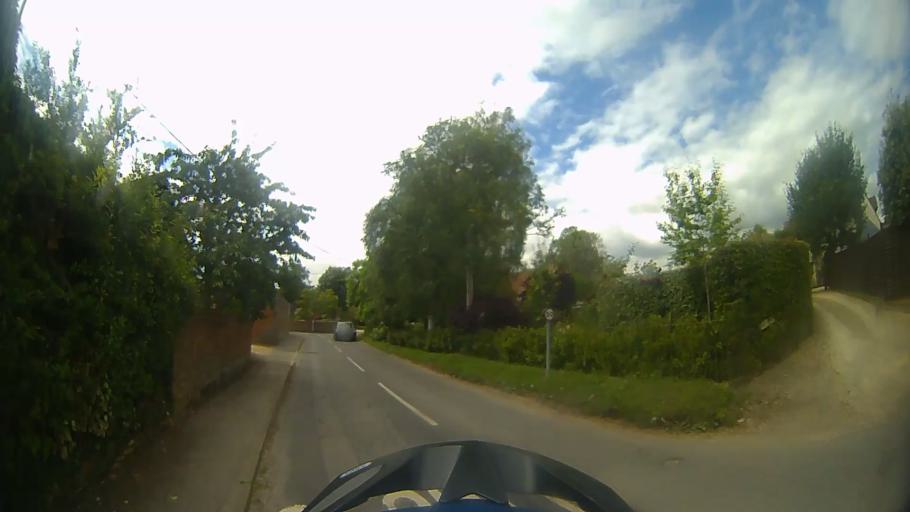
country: GB
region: England
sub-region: Oxfordshire
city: Wantage
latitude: 51.5773
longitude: -1.4507
